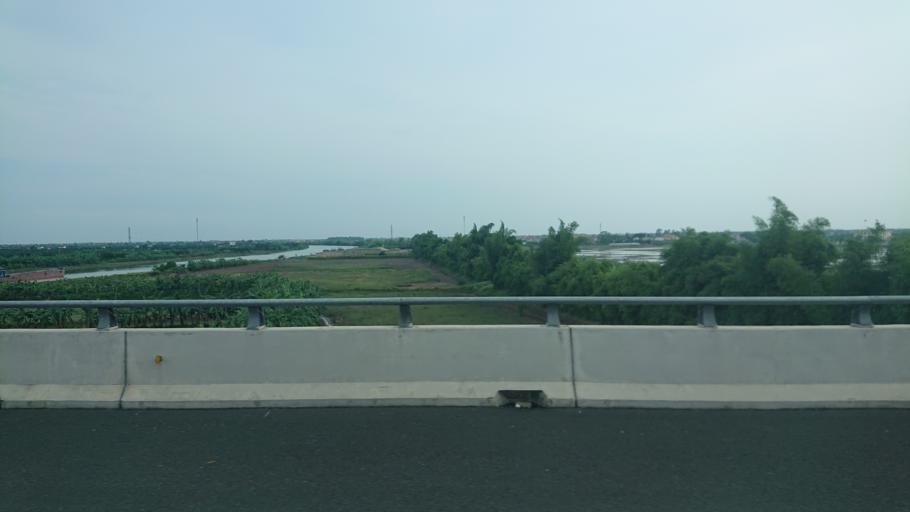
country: VN
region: Hai Duong
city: Tu Ky
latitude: 20.8333
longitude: 106.4406
